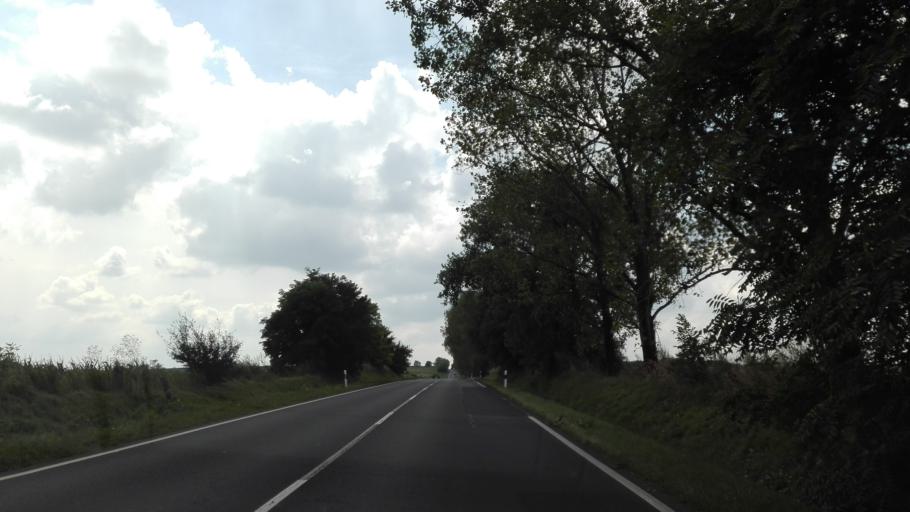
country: HU
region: Fejer
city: Eloszallas
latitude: 46.8304
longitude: 18.8108
